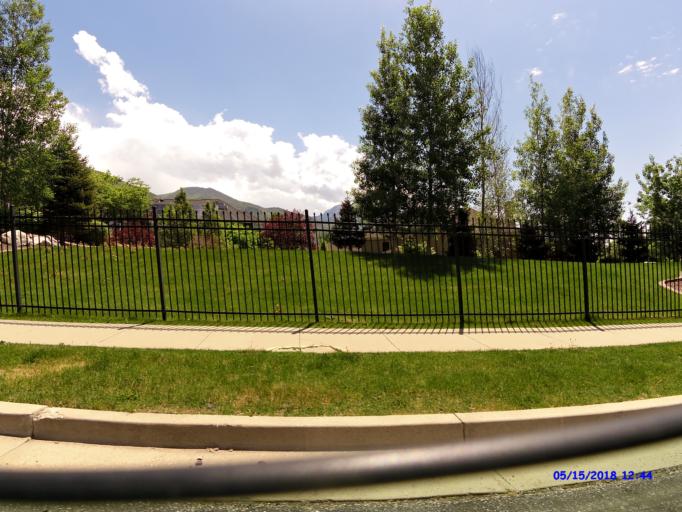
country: US
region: Utah
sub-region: Weber County
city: Uintah
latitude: 41.1623
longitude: -111.9249
